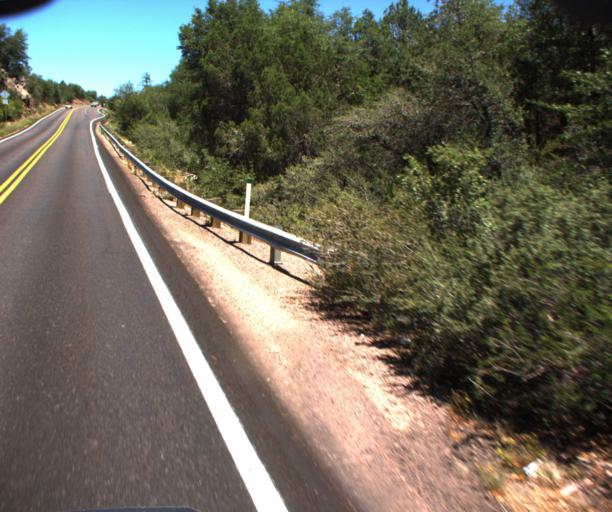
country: US
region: Arizona
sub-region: Gila County
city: Pine
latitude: 34.3208
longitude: -111.4157
